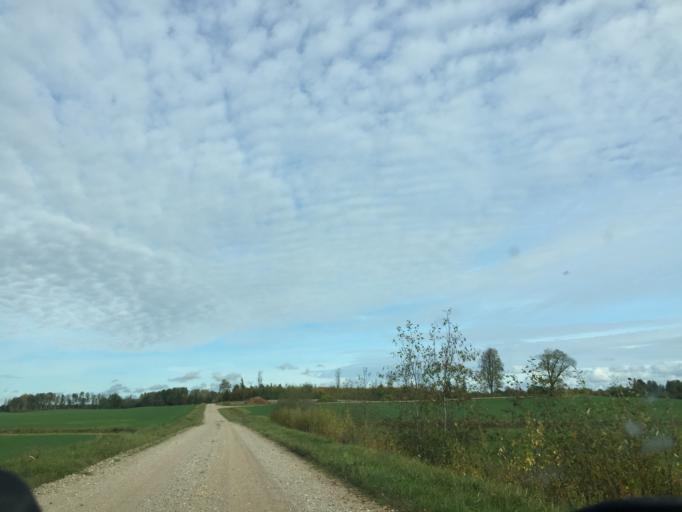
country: LV
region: Jaunpils
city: Jaunpils
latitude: 56.6293
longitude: 23.0642
